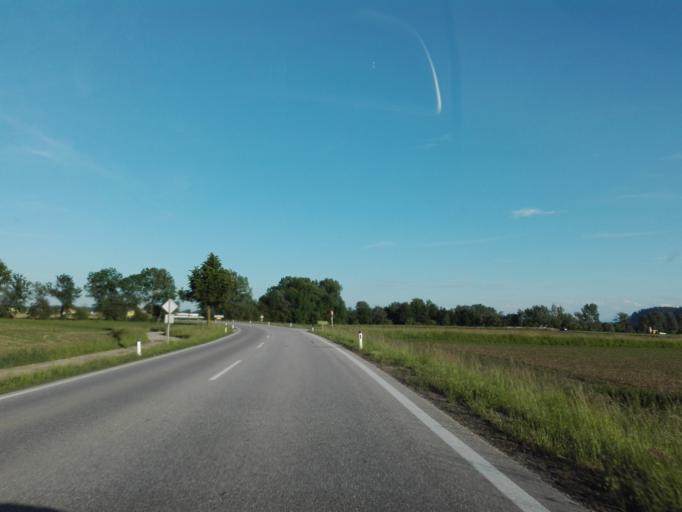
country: AT
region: Upper Austria
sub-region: Politischer Bezirk Urfahr-Umgebung
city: Feldkirchen an der Donau
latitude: 48.3649
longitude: 13.9846
